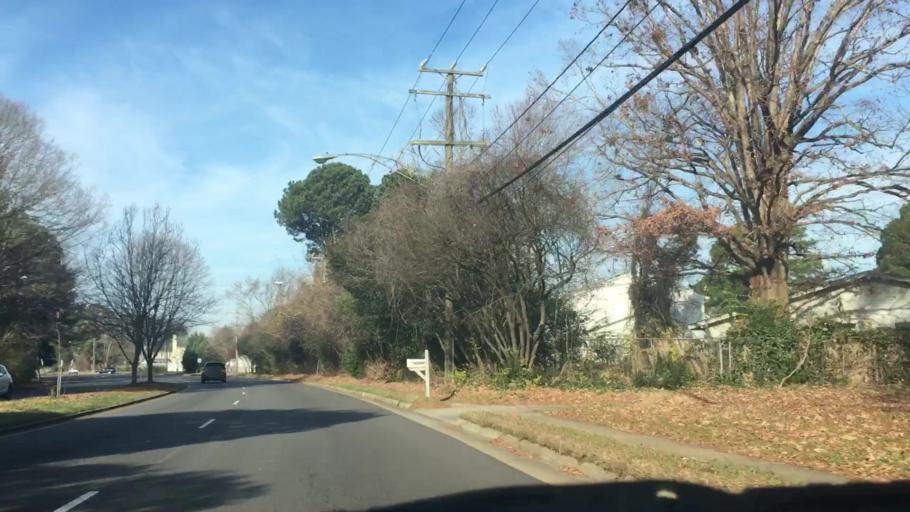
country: US
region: Virginia
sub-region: City of Chesapeake
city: Chesapeake
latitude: 36.8241
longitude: -76.1534
